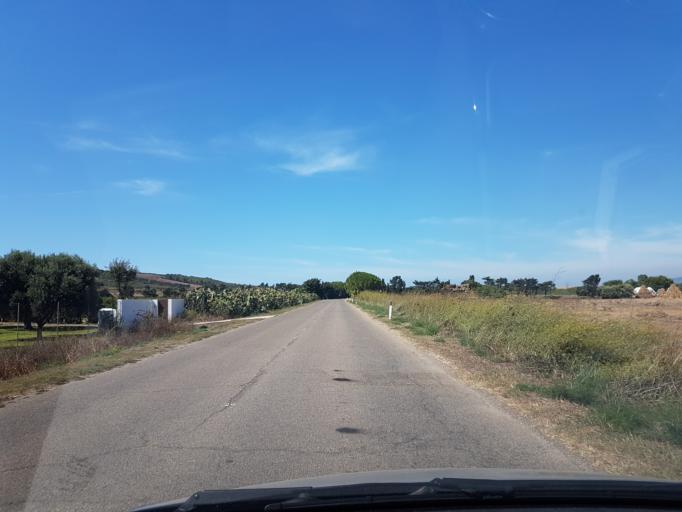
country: IT
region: Sardinia
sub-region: Provincia di Oristano
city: Cabras
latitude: 39.9413
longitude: 8.4576
